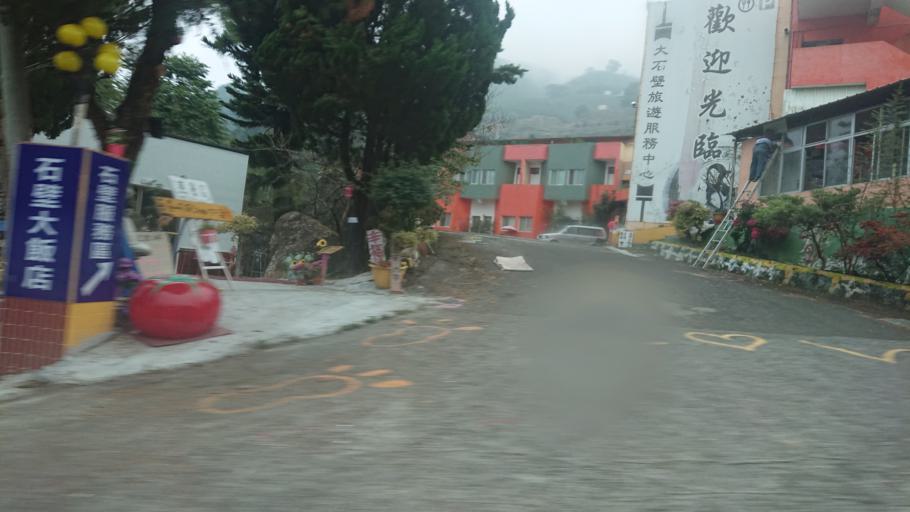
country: TW
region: Taiwan
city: Lugu
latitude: 23.6059
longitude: 120.7083
